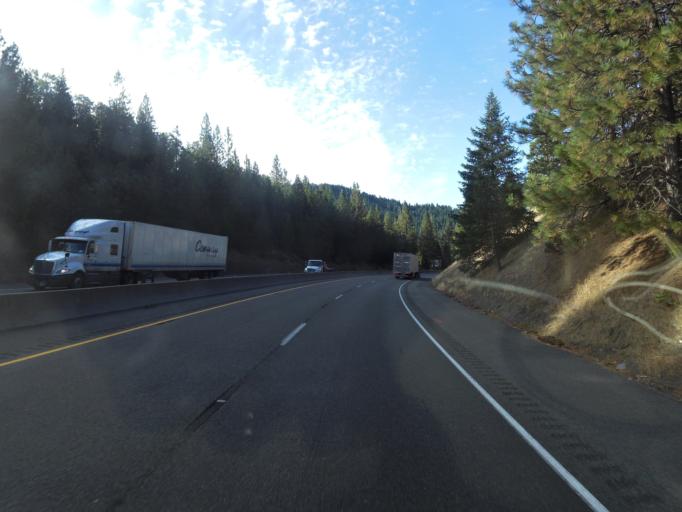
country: US
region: California
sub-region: Siskiyou County
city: Dunsmuir
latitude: 41.1551
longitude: -122.2944
